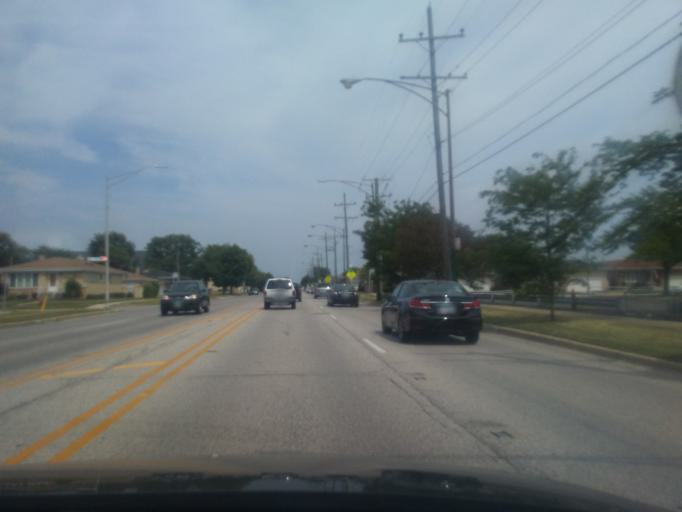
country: US
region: Illinois
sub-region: Cook County
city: Norridge
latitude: 41.9664
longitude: -87.8446
